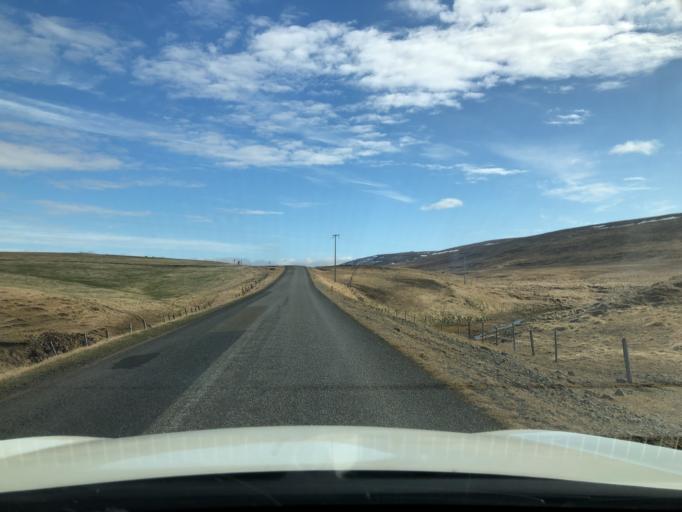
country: IS
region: West
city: Borgarnes
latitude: 65.1091
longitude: -21.6969
